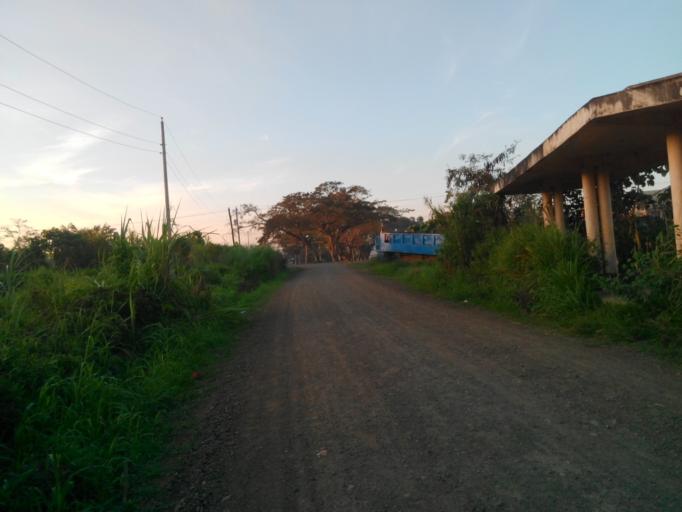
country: PH
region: Western Visayas
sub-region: Province of Iloilo
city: Passi
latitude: 11.1185
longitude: 122.6470
